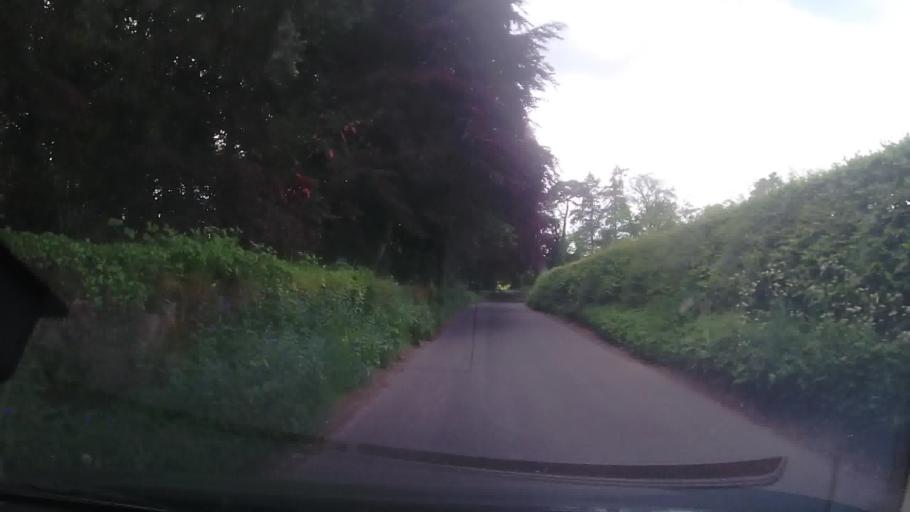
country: GB
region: England
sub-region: Shropshire
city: Clive
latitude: 52.8035
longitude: -2.7214
